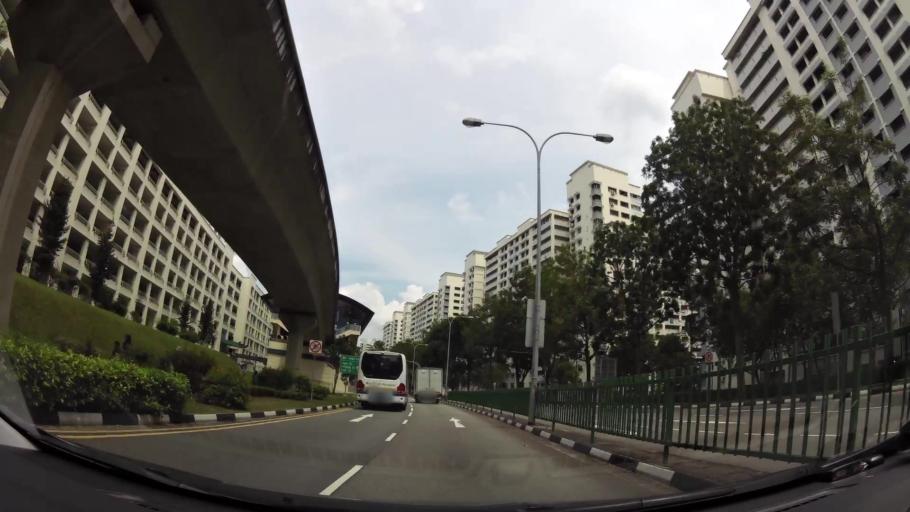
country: MY
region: Johor
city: Johor Bahru
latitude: 1.3862
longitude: 103.7640
